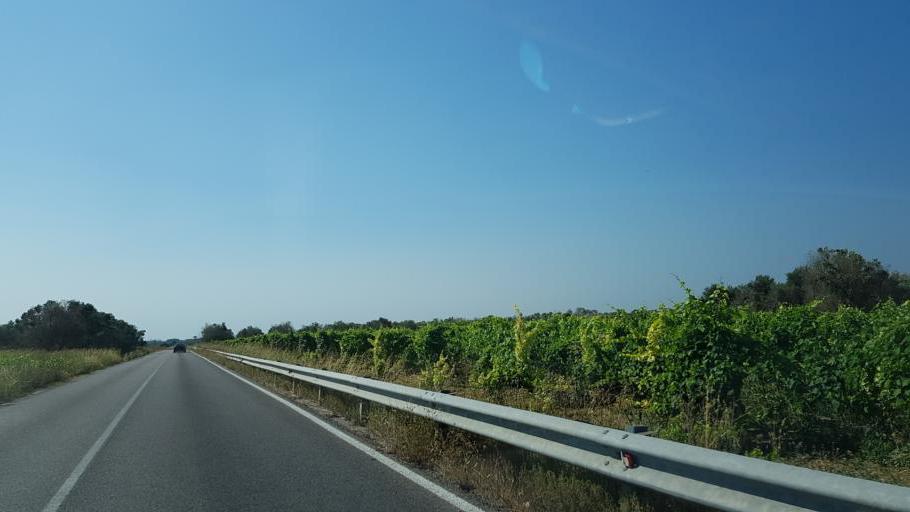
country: IT
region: Apulia
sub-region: Provincia di Brindisi
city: San Donaci
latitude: 40.4307
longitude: 17.9405
